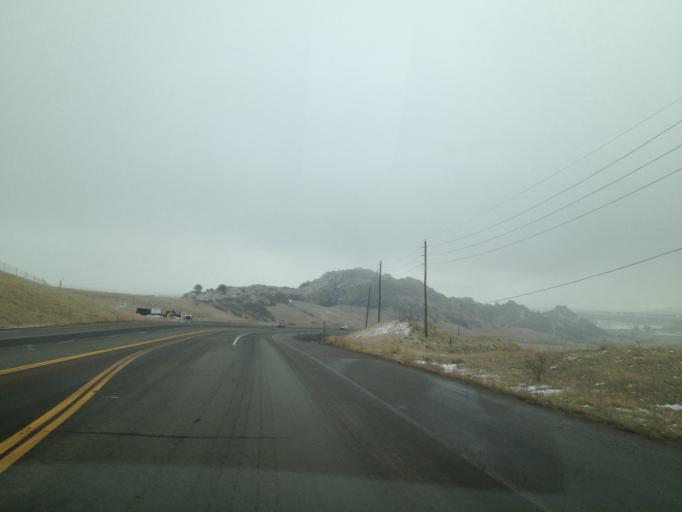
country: US
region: Colorado
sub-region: Jefferson County
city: Golden
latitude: 39.8582
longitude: -105.2339
